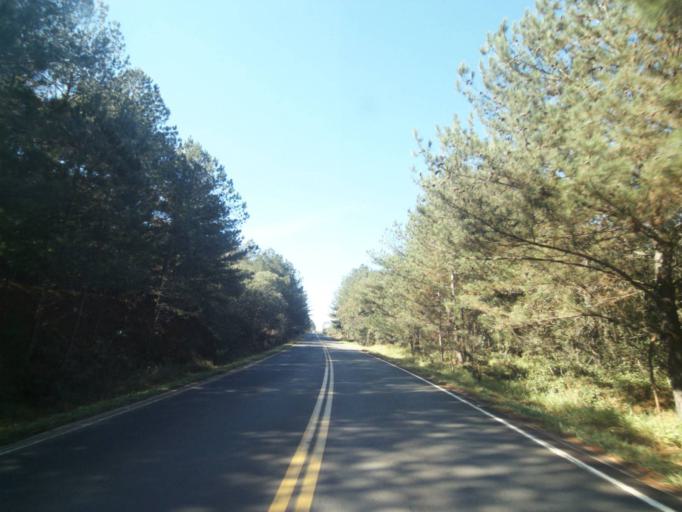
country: BR
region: Parana
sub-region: Tibagi
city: Tibagi
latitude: -24.4779
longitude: -50.4840
